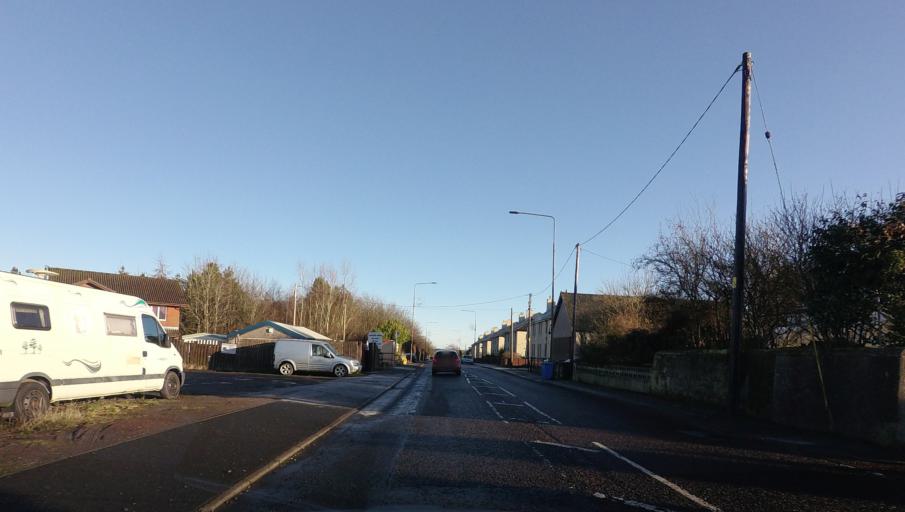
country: GB
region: Scotland
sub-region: West Lothian
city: Blackburn
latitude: 55.8295
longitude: -3.6573
